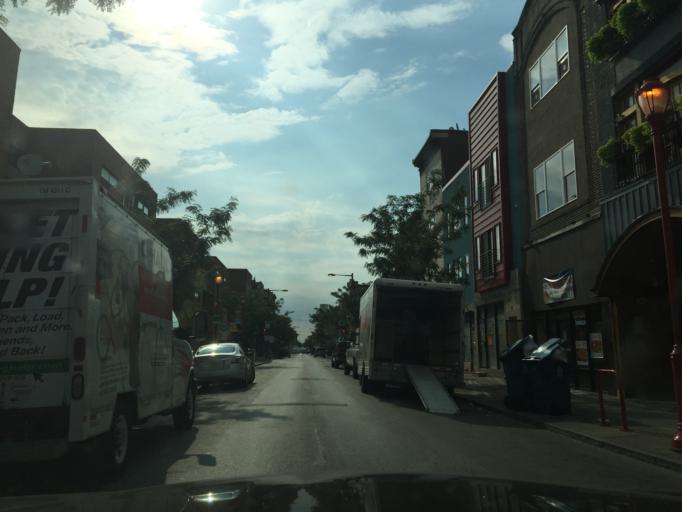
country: US
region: Pennsylvania
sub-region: Philadelphia County
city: Philadelphia
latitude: 39.9423
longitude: -75.1548
